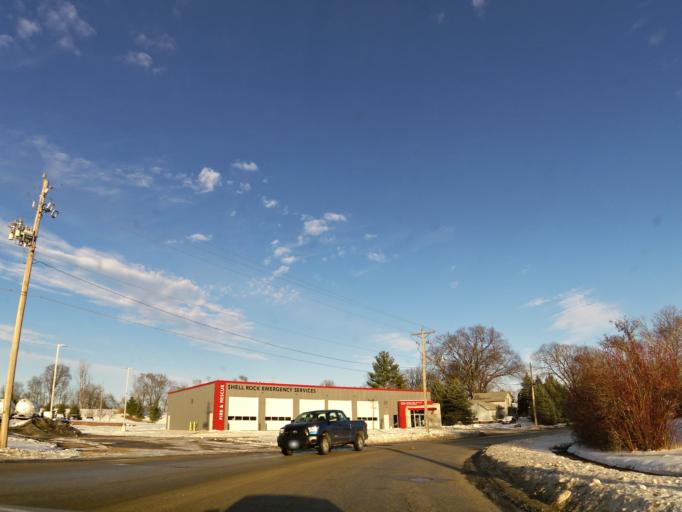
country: US
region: Iowa
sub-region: Butler County
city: Shell Rock
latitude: 42.7147
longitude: -92.5780
